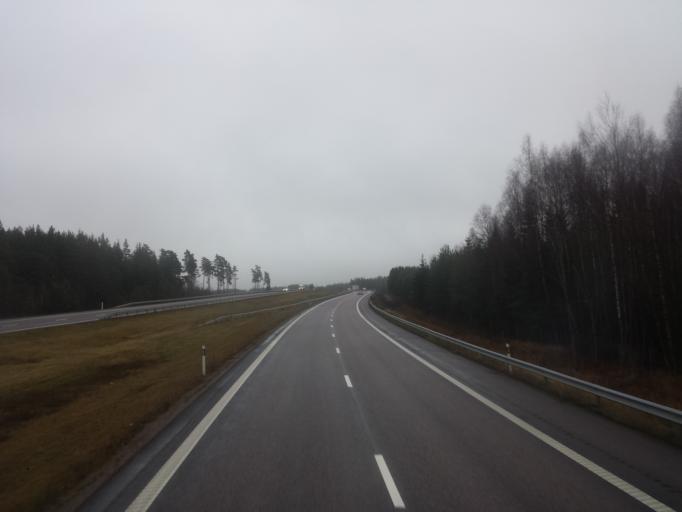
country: SE
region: Soedermanland
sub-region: Nykopings Kommun
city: Svalsta
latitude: 58.7546
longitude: 16.8681
